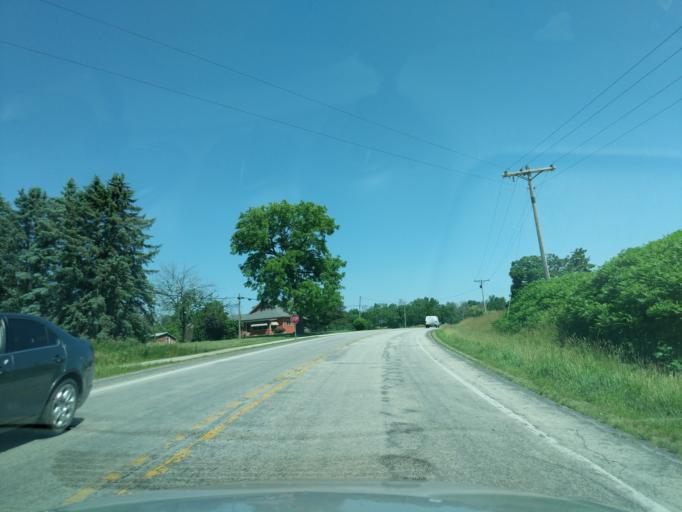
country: US
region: Indiana
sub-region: Whitley County
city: Columbia City
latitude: 41.1222
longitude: -85.4809
